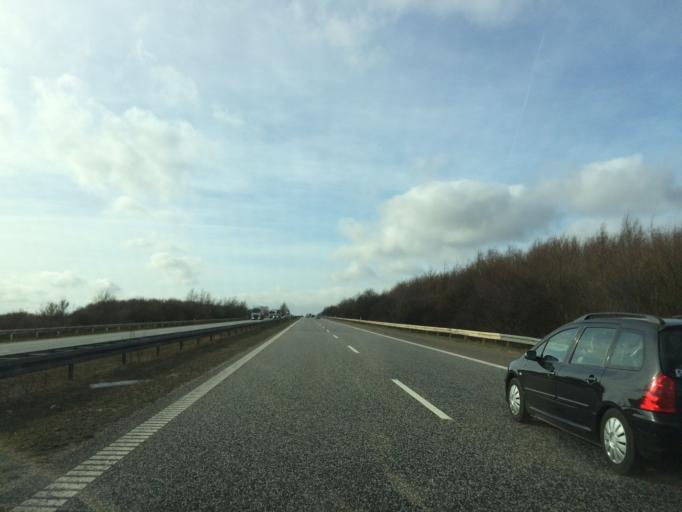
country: DK
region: Central Jutland
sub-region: Randers Kommune
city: Randers
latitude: 56.4285
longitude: 10.0432
